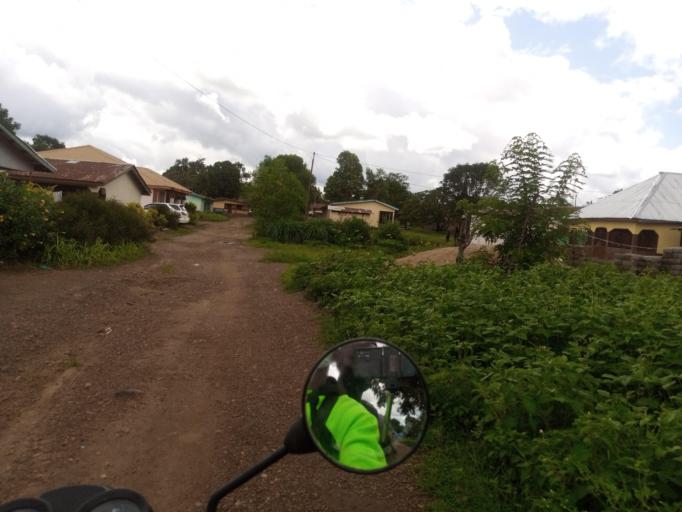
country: SL
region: Northern Province
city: Port Loko
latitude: 8.7638
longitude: -12.7795
